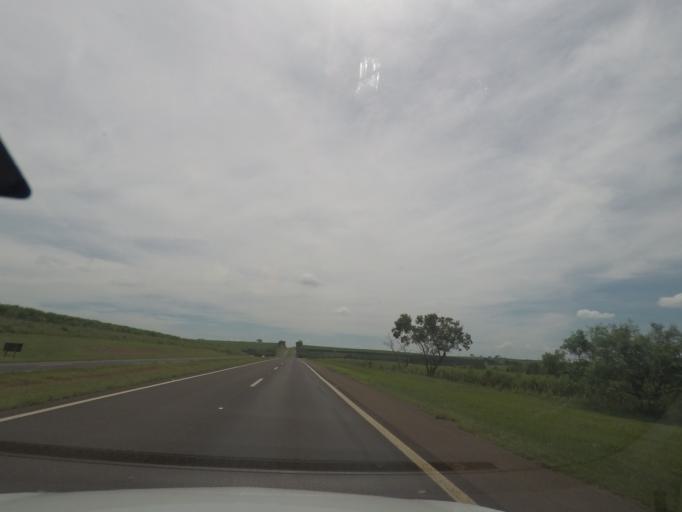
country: BR
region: Sao Paulo
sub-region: Bebedouro
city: Bebedouro
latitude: -21.0345
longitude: -48.4195
